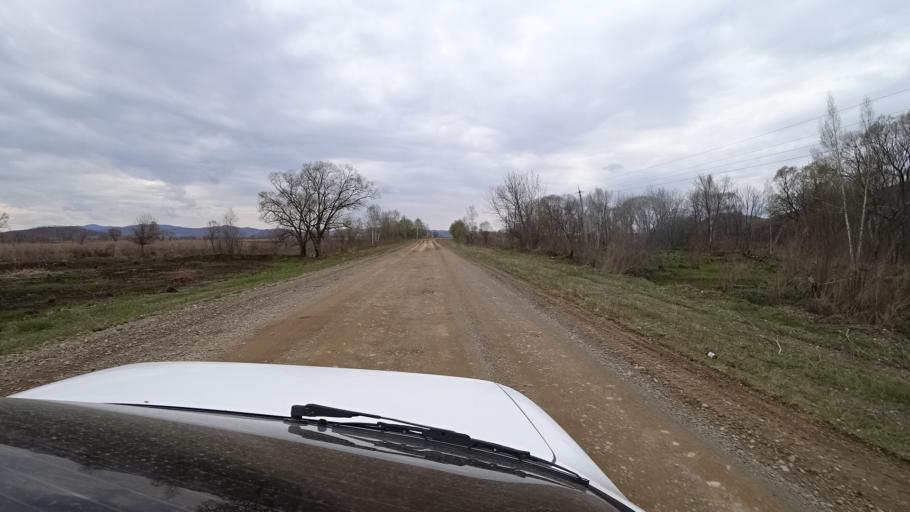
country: RU
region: Primorskiy
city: Novopokrovka
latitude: 45.5627
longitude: 134.3330
